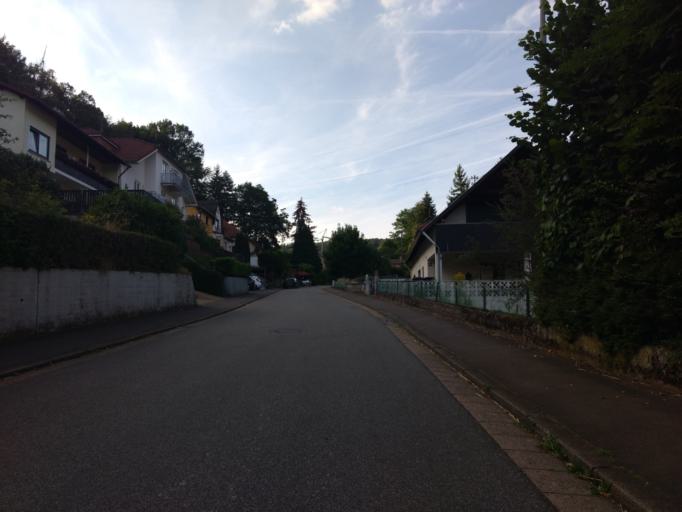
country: DE
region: Saarland
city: Beckingen
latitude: 49.3975
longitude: 6.7005
